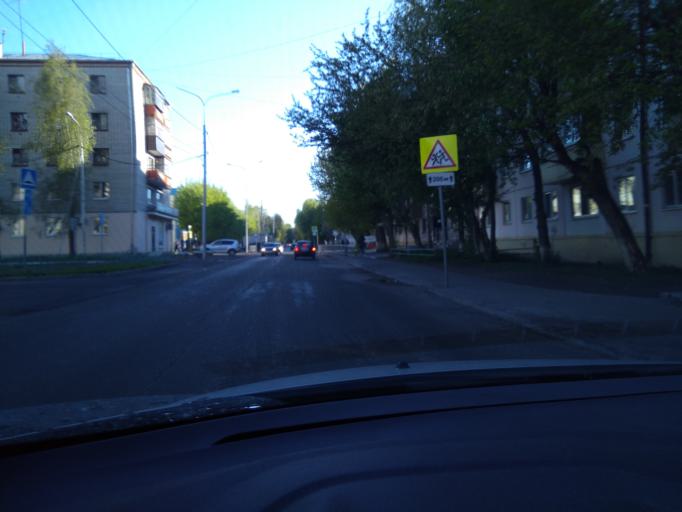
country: RU
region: Tjumen
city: Tyumen
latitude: 57.1347
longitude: 65.5939
